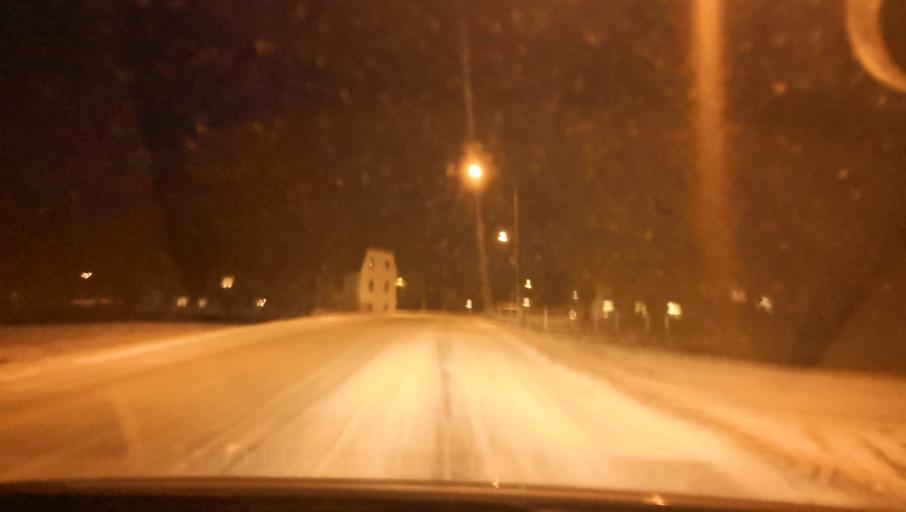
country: SE
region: Uppsala
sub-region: Heby Kommun
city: Tarnsjo
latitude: 60.2906
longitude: 16.8853
